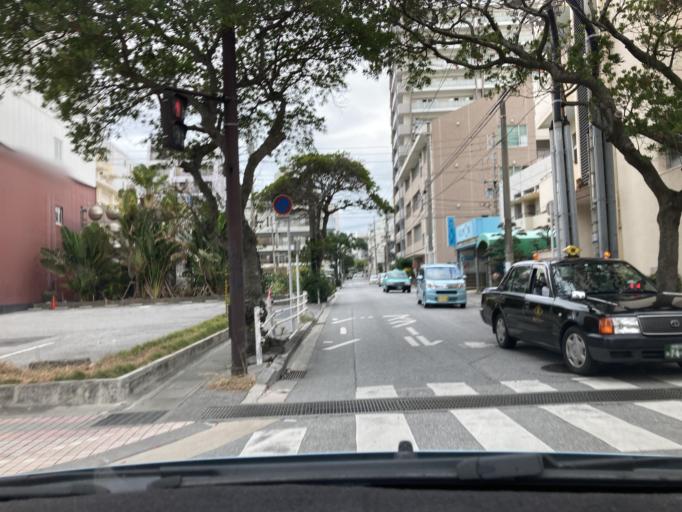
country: JP
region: Okinawa
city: Naha-shi
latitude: 26.2123
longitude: 127.6728
